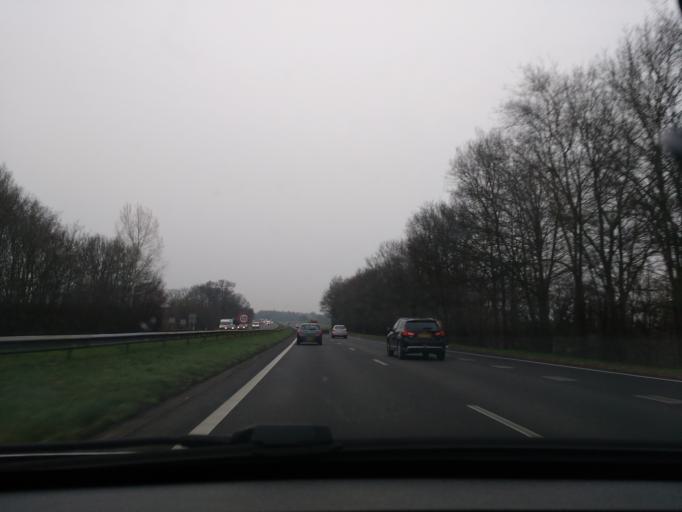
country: NL
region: Gelderland
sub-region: Gemeente Barneveld
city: Barneveld
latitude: 52.1208
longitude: 5.5665
